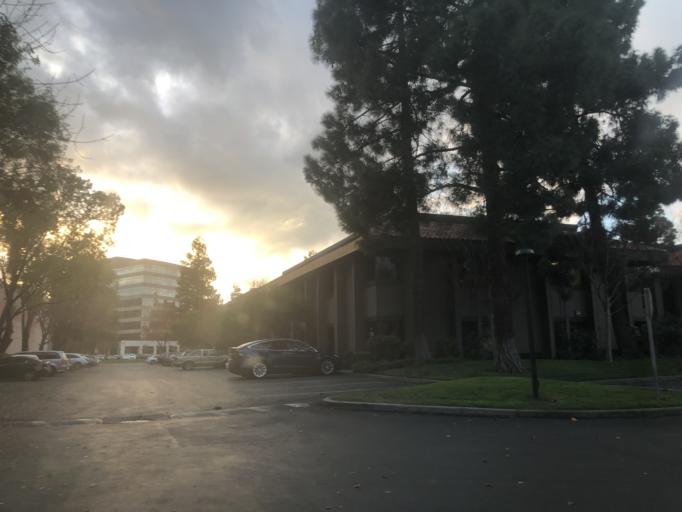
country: US
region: California
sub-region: Santa Clara County
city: San Jose
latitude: 37.3694
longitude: -121.9183
